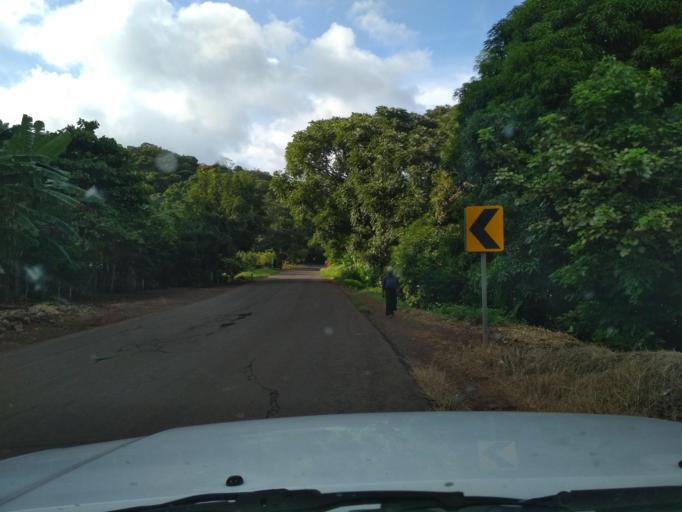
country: MX
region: Veracruz
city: Catemaco
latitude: 18.3873
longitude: -95.1226
